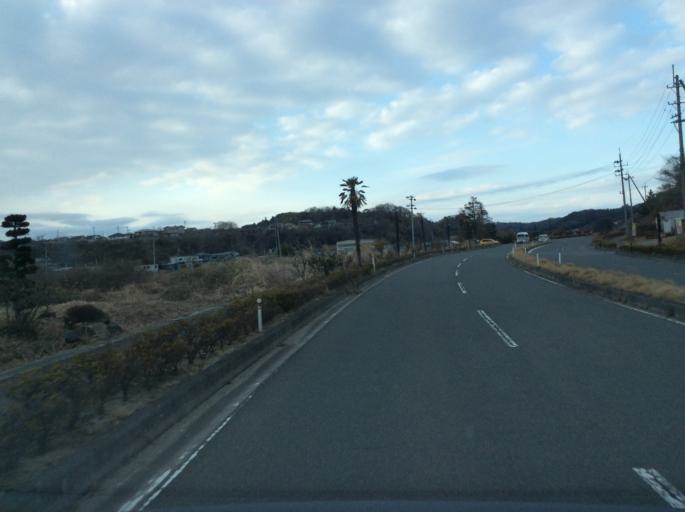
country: JP
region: Fukushima
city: Iwaki
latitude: 36.9560
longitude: 140.9190
